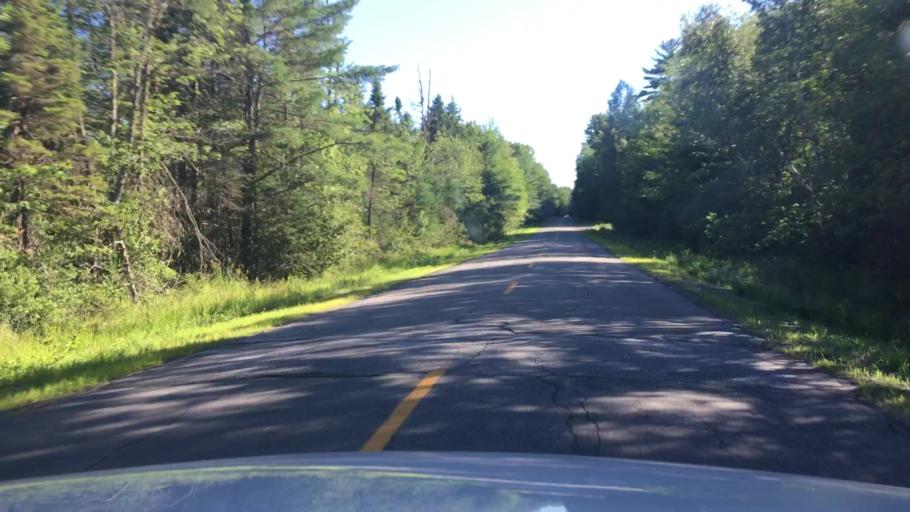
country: US
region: Maine
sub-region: Penobscot County
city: Enfield
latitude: 45.2160
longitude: -68.5851
